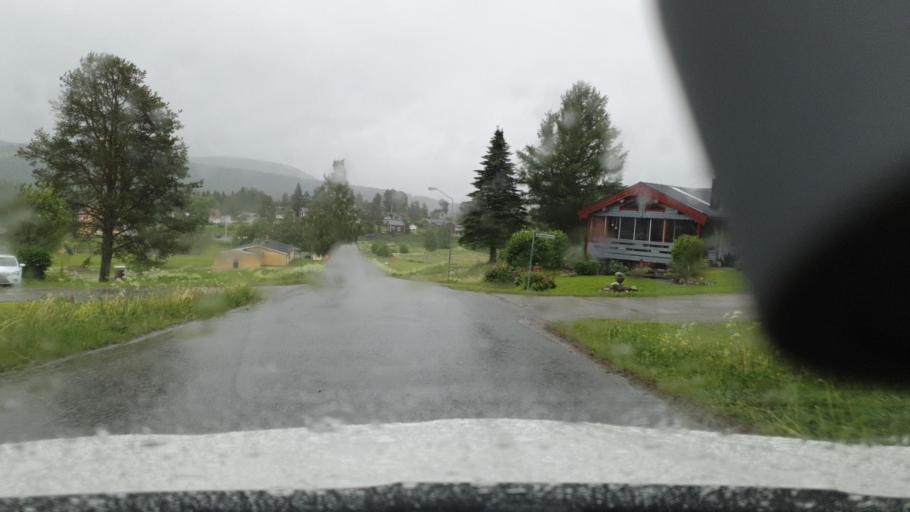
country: SE
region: Vaesterbotten
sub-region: Skelleftea Kommun
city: Burtraesk
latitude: 64.3473
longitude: 20.4980
